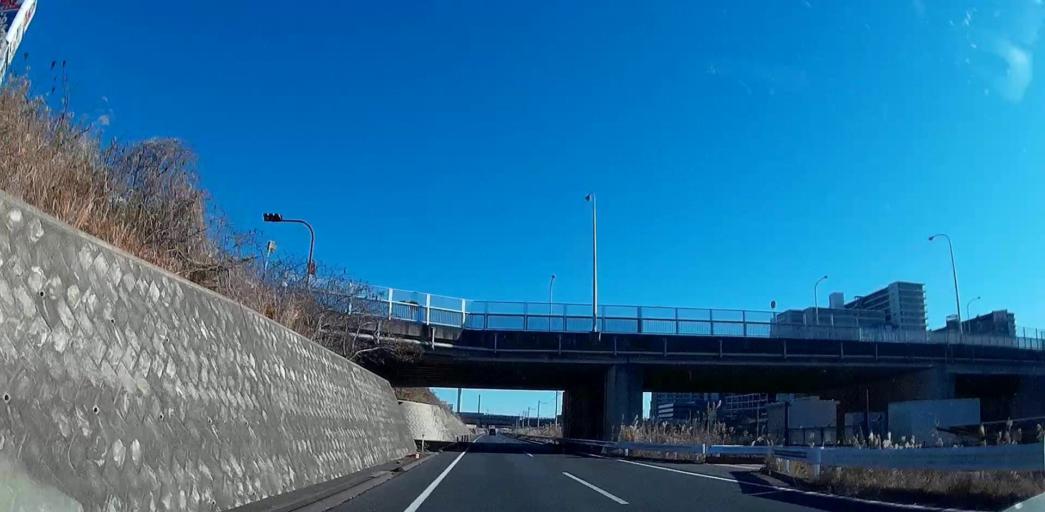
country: JP
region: Chiba
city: Shiroi
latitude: 35.7991
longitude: 140.1111
